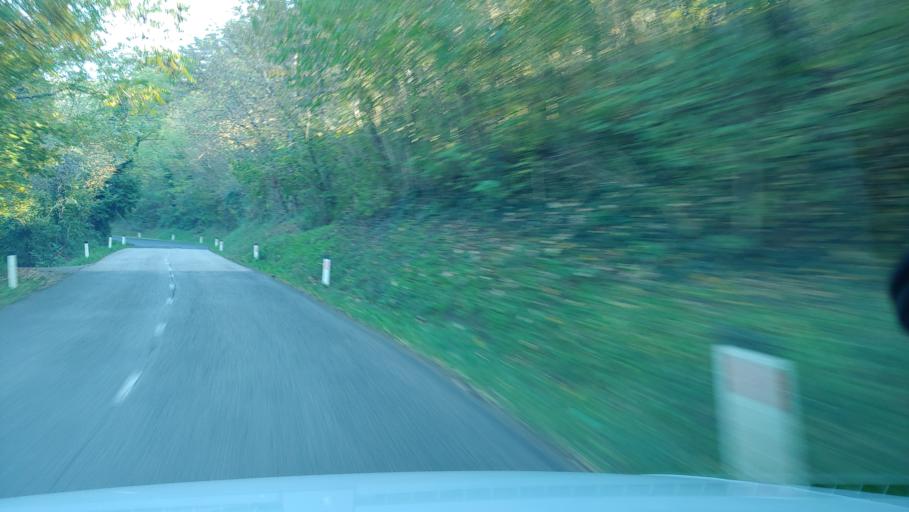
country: SI
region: Vipava
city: Vipava
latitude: 45.8130
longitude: 13.9080
